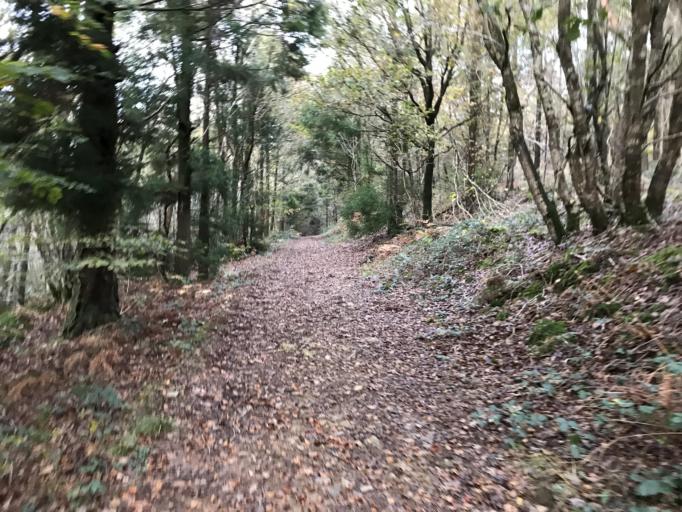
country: FR
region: Brittany
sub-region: Departement du Finistere
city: Hopital-Camfrout
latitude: 48.3321
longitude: -4.2249
